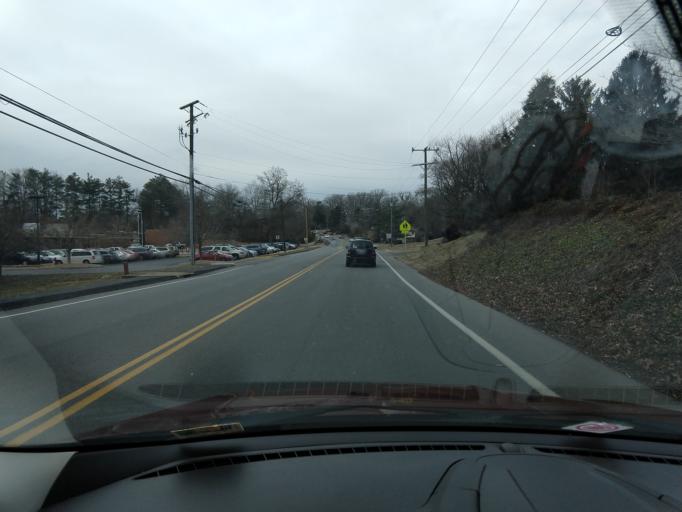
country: US
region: Virginia
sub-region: City of Waynesboro
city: Waynesboro
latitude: 38.0703
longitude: -78.9095
